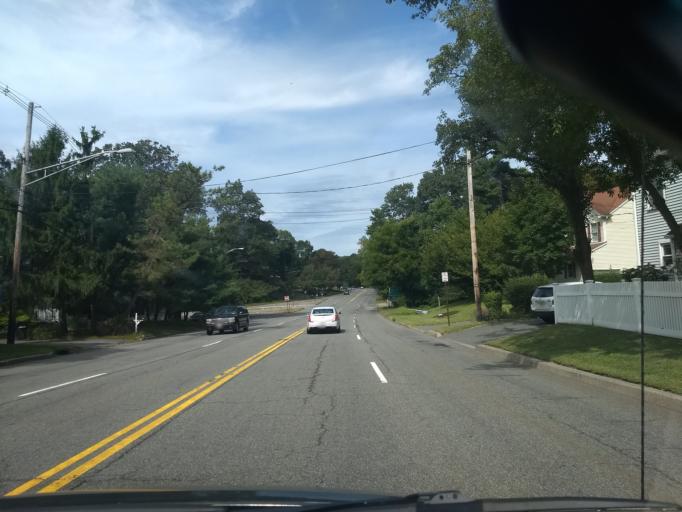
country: US
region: New Jersey
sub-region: Morris County
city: Morris Plains
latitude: 40.8244
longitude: -74.4927
